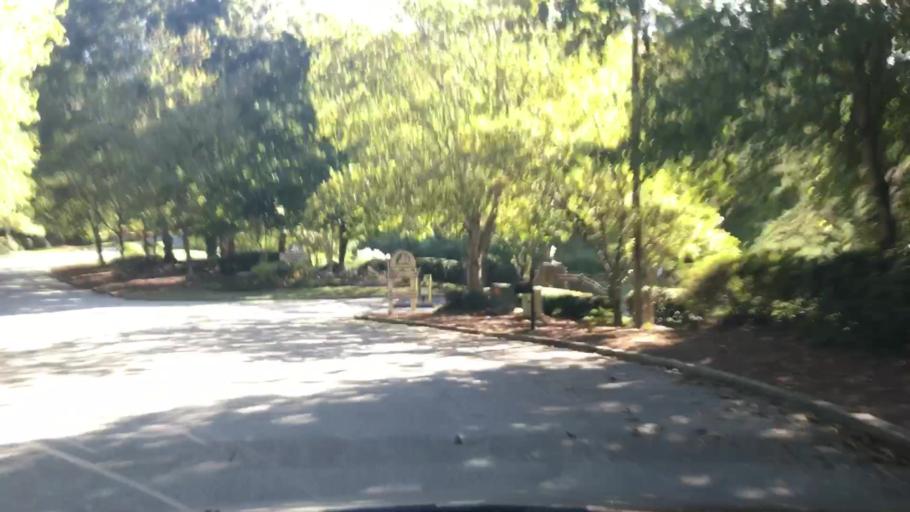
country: US
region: Georgia
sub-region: DeKalb County
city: Redan
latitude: 33.7925
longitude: -84.0980
